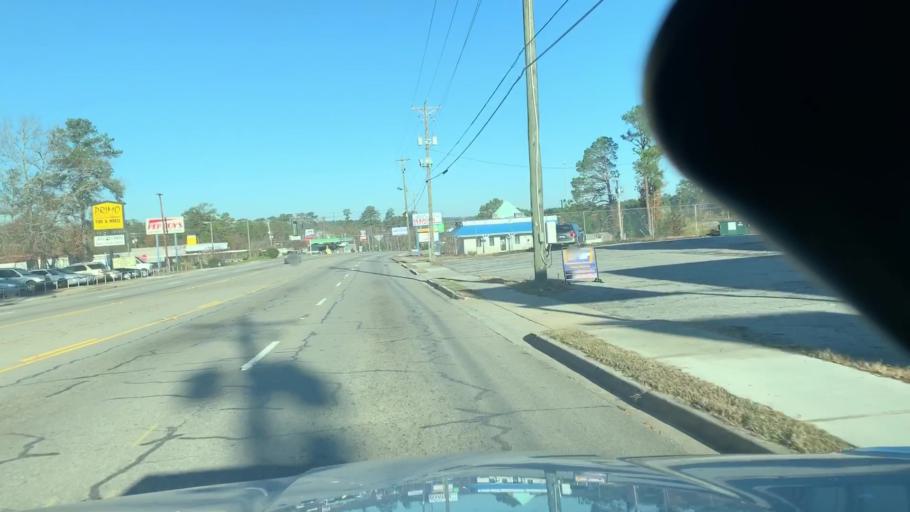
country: US
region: South Carolina
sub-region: Richland County
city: Dentsville
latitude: 34.0563
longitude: -80.9489
